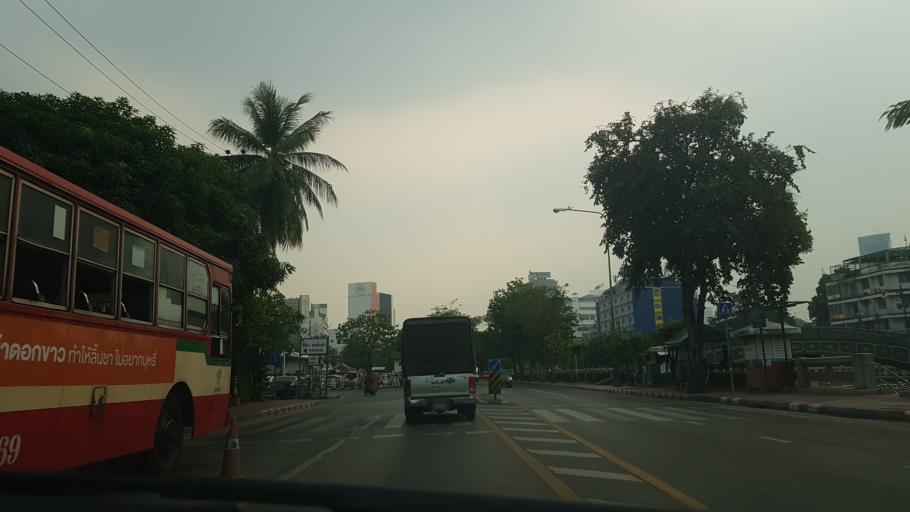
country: TH
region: Bangkok
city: Pathum Wan
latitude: 13.7412
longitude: 100.5160
